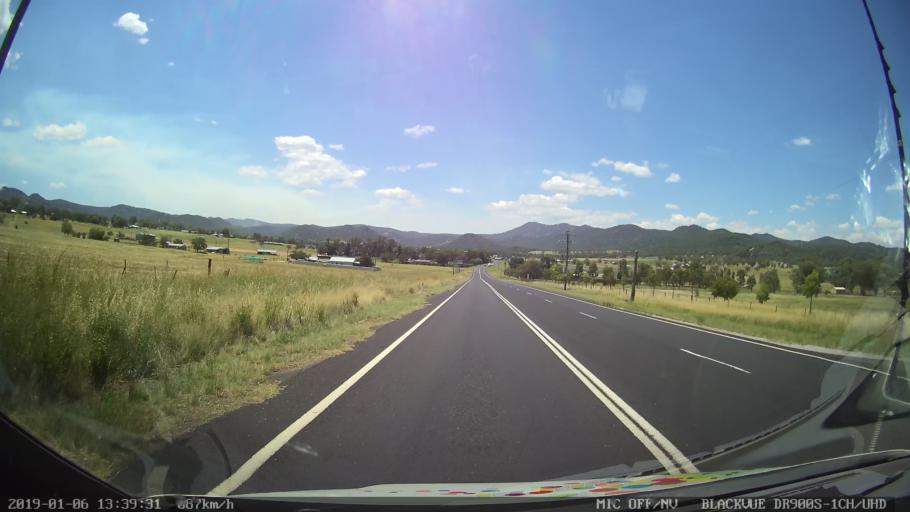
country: AU
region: New South Wales
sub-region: Tamworth Municipality
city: Kootingal
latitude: -31.0348
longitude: 151.0620
